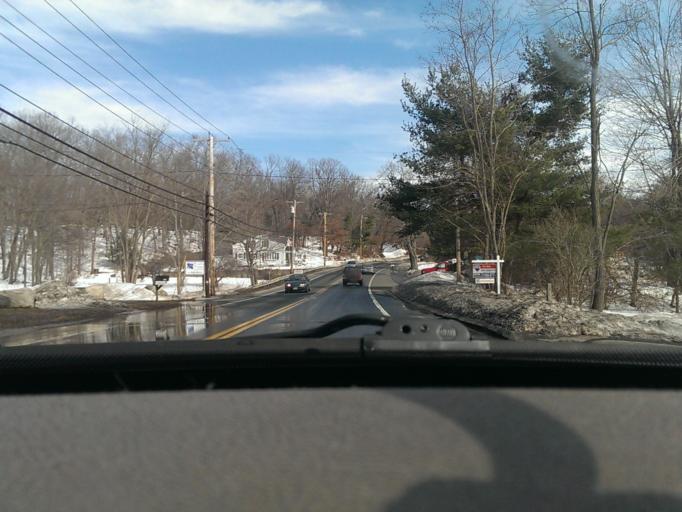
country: US
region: Massachusetts
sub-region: Hampden County
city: Three Rivers
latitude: 42.1524
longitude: -72.3846
